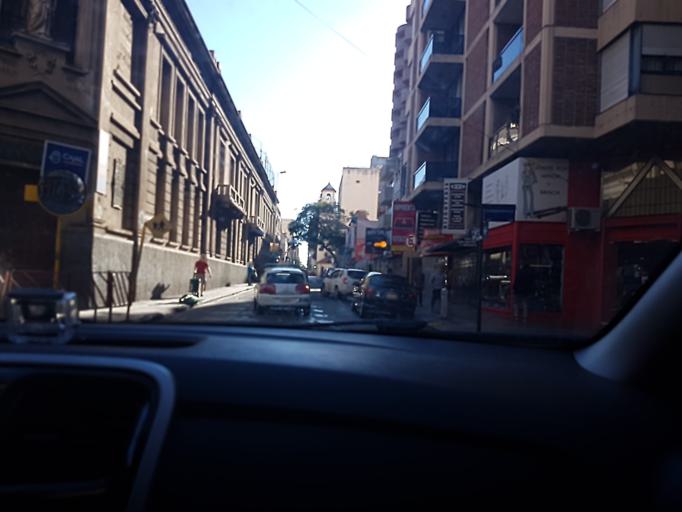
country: AR
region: Cordoba
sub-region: Departamento de Capital
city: Cordoba
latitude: -31.4193
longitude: -64.1855
